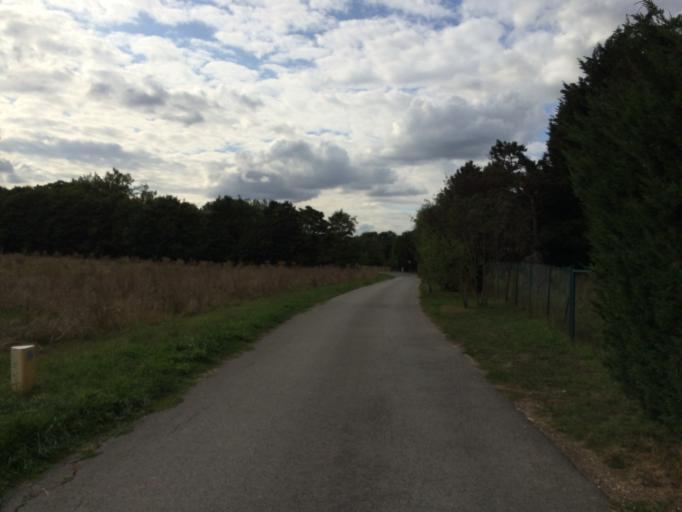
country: FR
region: Ile-de-France
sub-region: Departement de l'Essonne
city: Soisy-sur-Seine
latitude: 48.6525
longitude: 2.4372
